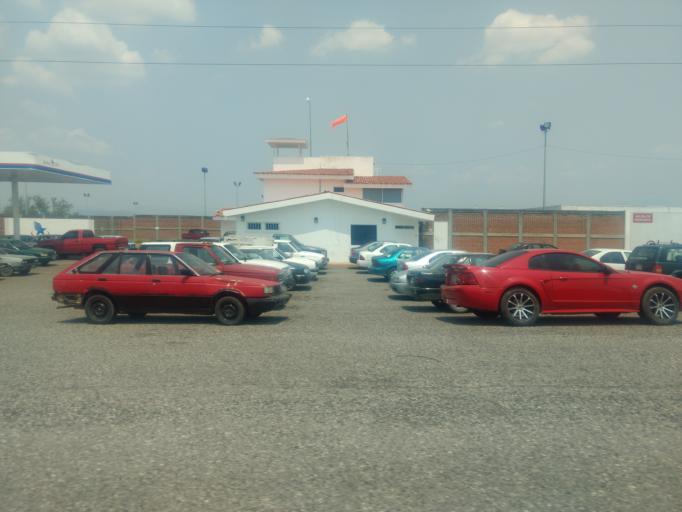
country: MX
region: Morelos
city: Ahuehuetzingo
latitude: 18.6908
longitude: -99.2837
